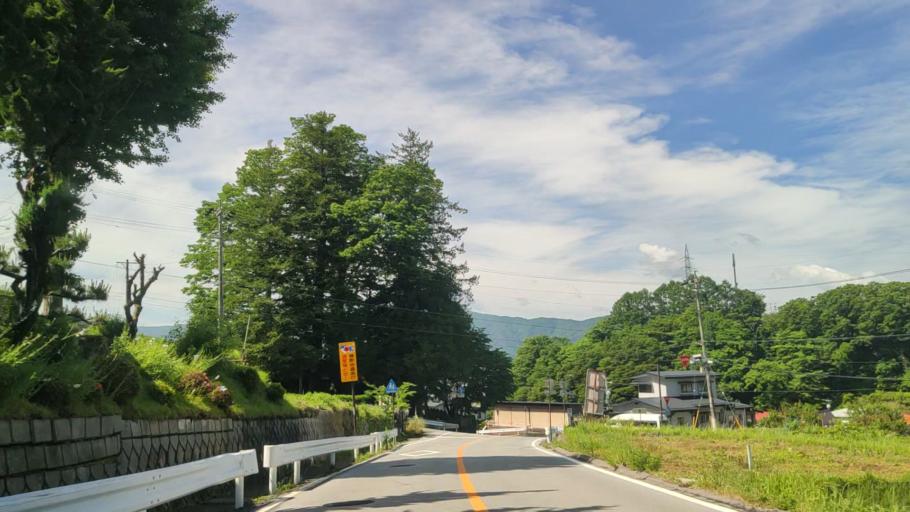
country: JP
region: Nagano
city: Suwa
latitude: 36.0501
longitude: 138.1276
